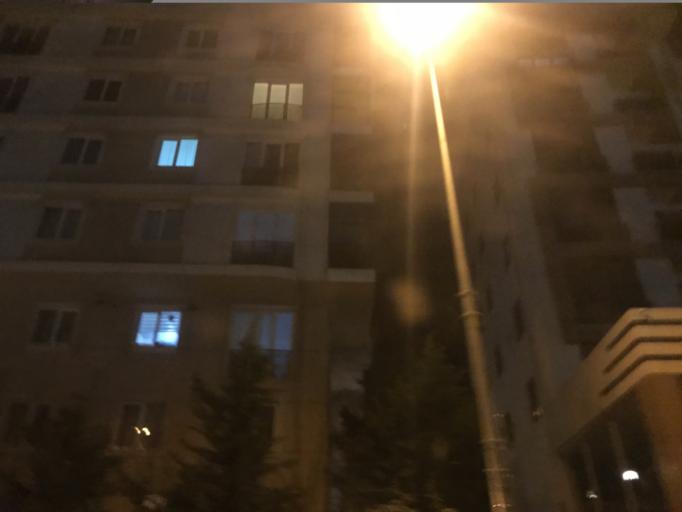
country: TR
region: Istanbul
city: Pendik
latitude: 40.8964
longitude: 29.2563
